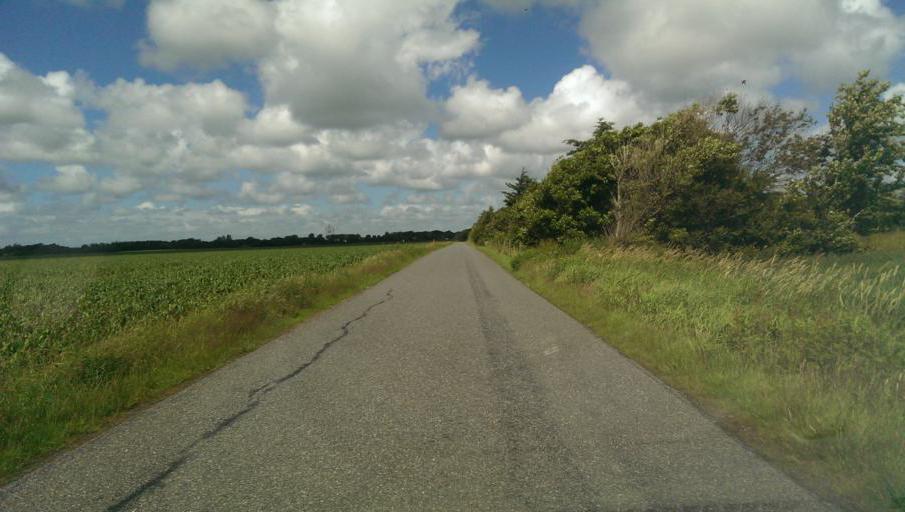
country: DK
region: Central Jutland
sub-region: Holstebro Kommune
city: Ulfborg
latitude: 56.2553
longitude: 8.2371
